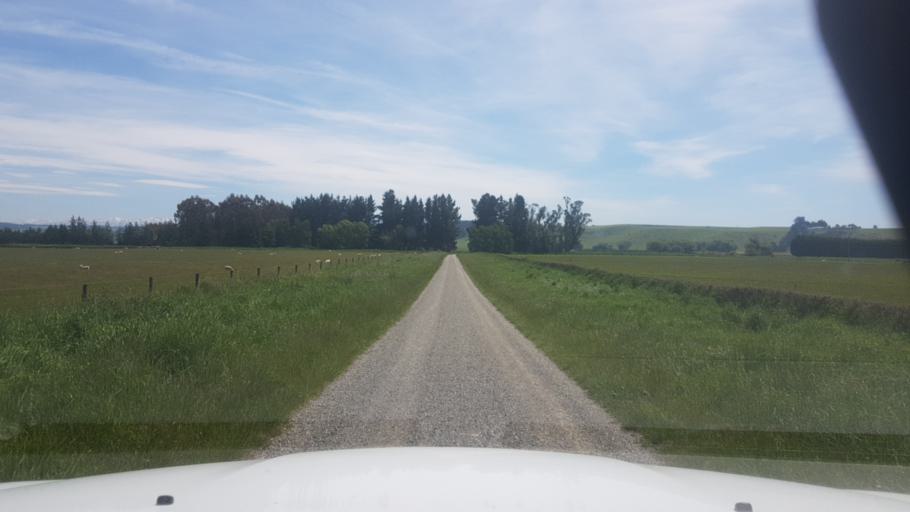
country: NZ
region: Canterbury
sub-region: Timaru District
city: Pleasant Point
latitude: -44.2235
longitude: 171.1637
